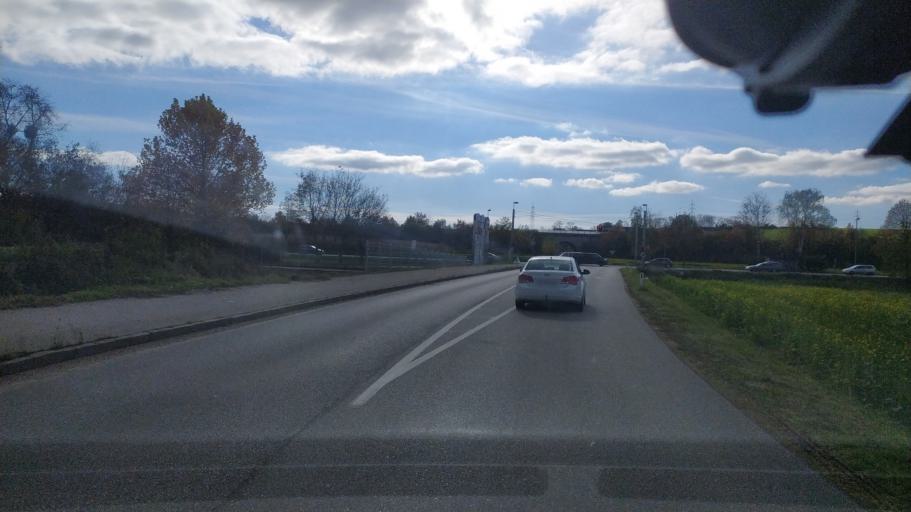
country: AT
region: Upper Austria
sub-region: Politischer Bezirk Linz-Land
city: Sankt Florian
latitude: 48.2357
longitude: 14.3754
